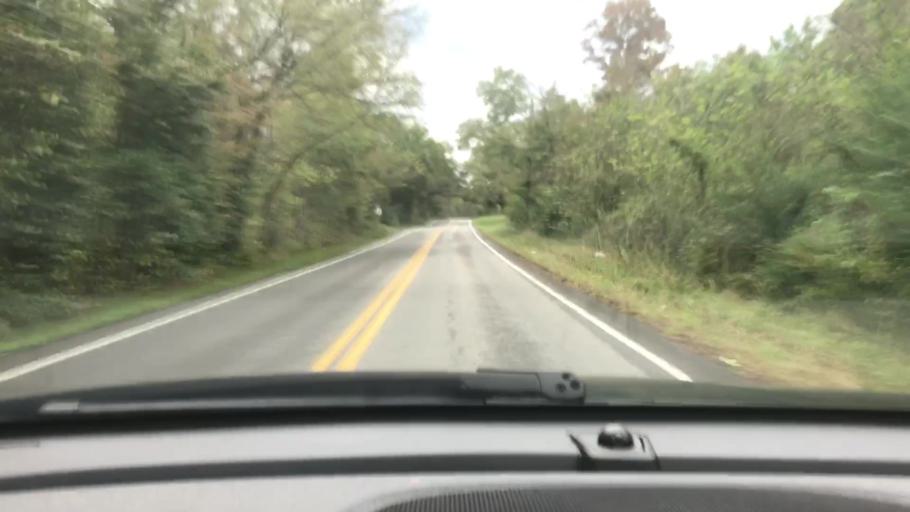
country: US
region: Tennessee
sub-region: Cheatham County
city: Ashland City
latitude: 36.2728
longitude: -87.1932
